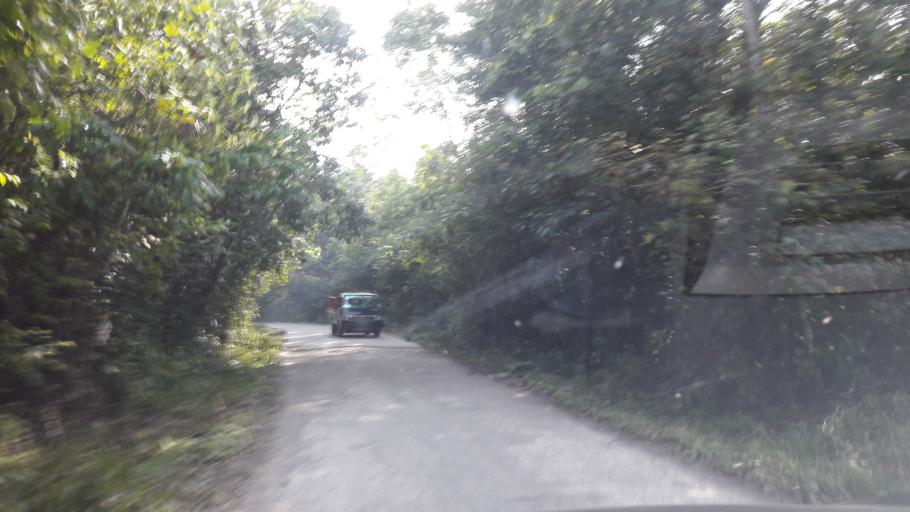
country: ID
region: South Sumatra
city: Gunungmenang
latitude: -3.1054
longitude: 103.9803
